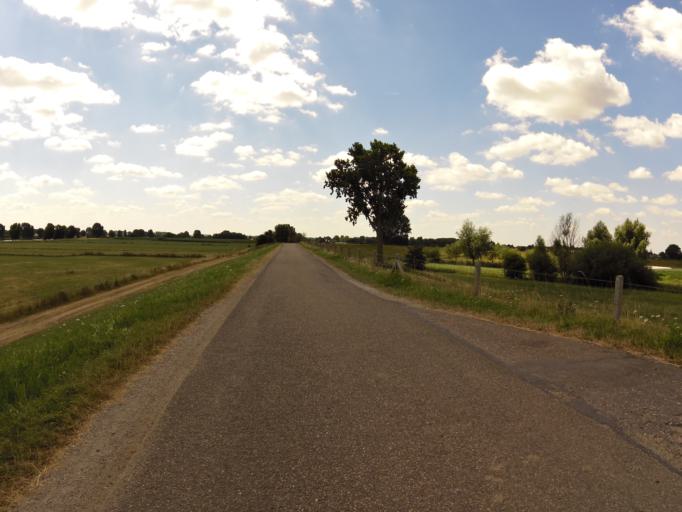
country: NL
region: Gelderland
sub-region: Gemeente Maasdriel
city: Heerewaarden
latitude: 51.7806
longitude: 5.3573
